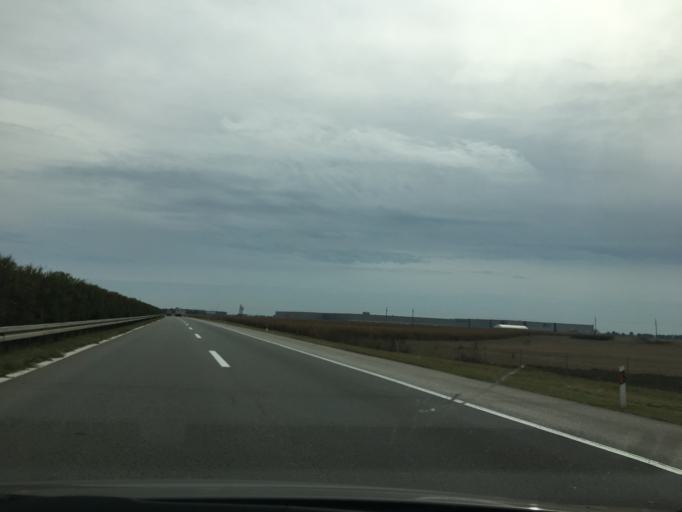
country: RS
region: Autonomna Pokrajina Vojvodina
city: Nova Pazova
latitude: 44.9779
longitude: 20.2240
